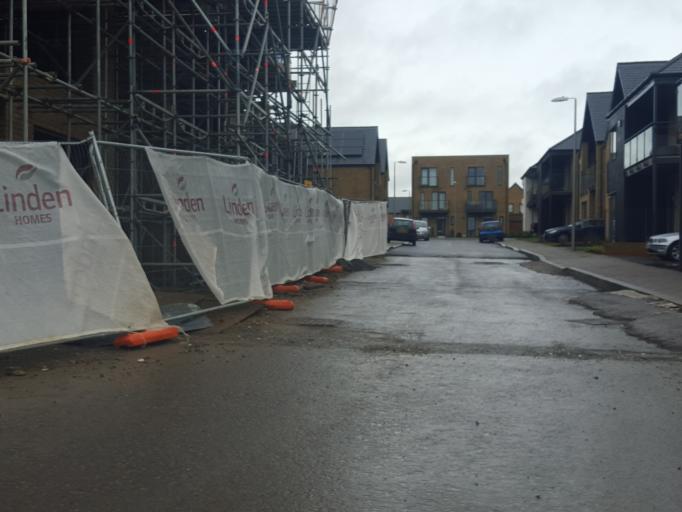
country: GB
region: England
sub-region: Essex
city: Harlow
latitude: 51.7709
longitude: 0.1408
